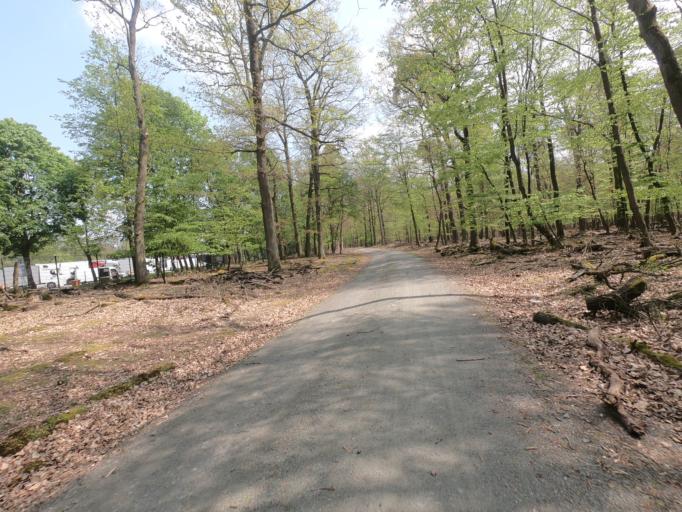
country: DE
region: Hesse
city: Niederrad
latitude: 50.0535
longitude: 8.6340
